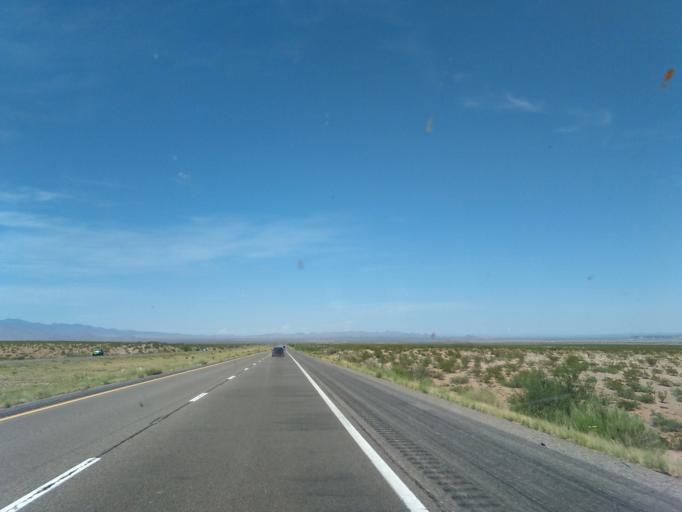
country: US
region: New Mexico
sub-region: Sierra County
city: Elephant Butte
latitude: 33.5614
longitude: -107.1763
